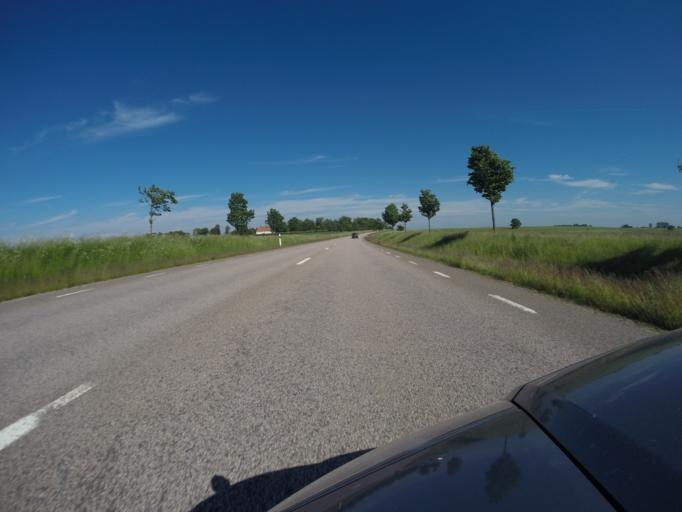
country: SE
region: Skane
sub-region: Bjuvs Kommun
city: Bjuv
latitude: 56.0126
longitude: 12.9292
